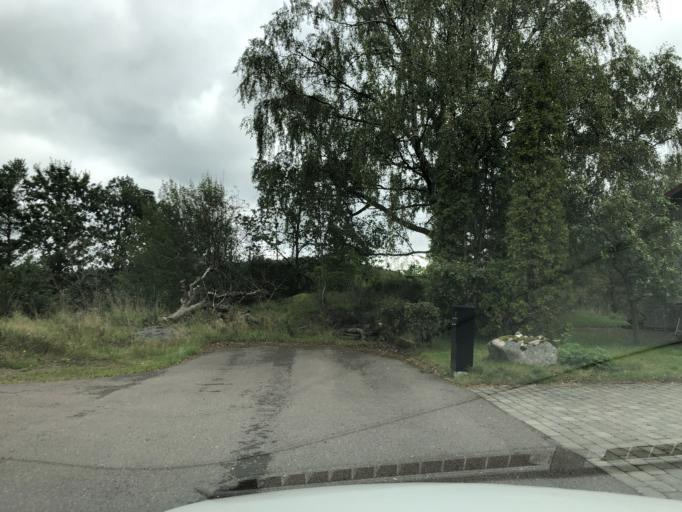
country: SE
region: Vaestra Goetaland
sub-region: Goteborg
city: Majorna
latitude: 57.7417
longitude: 11.9230
